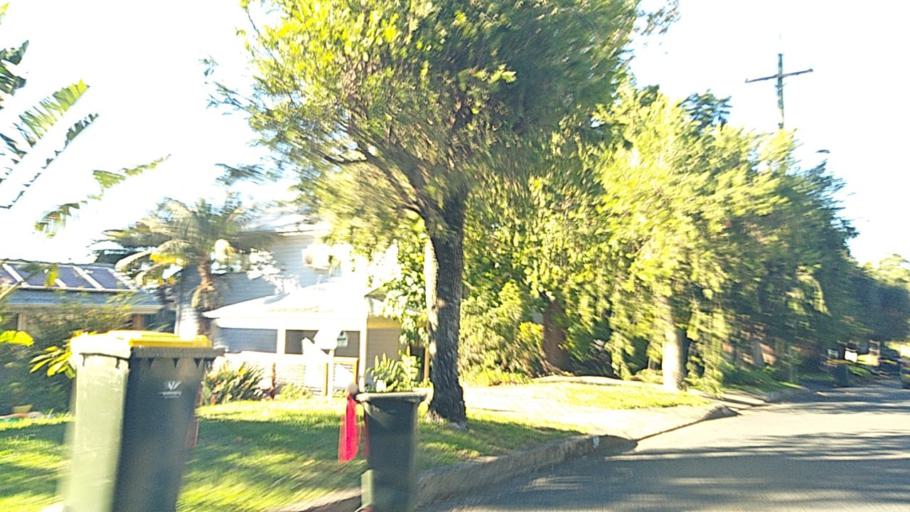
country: AU
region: New South Wales
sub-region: Wollongong
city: Bulli
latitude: -34.3107
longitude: 150.9170
